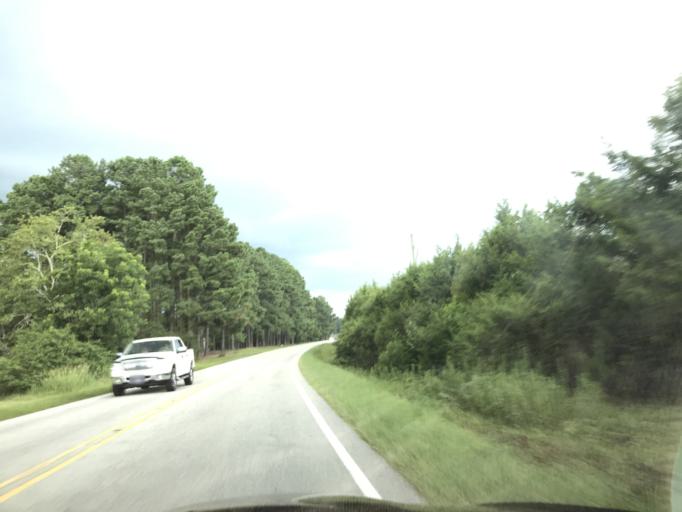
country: US
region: North Carolina
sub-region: Johnston County
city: Four Oaks
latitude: 35.5150
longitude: -78.5014
